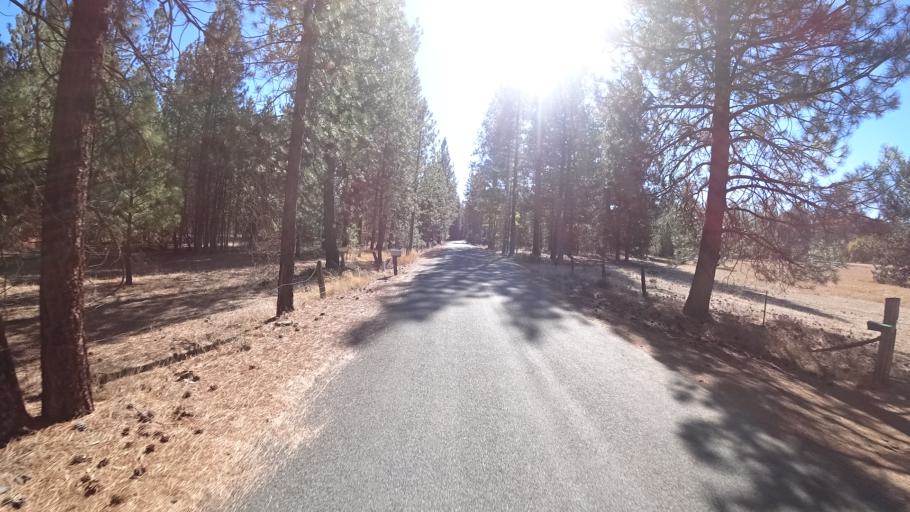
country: US
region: California
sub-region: Siskiyou County
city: Yreka
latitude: 41.5876
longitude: -122.9114
